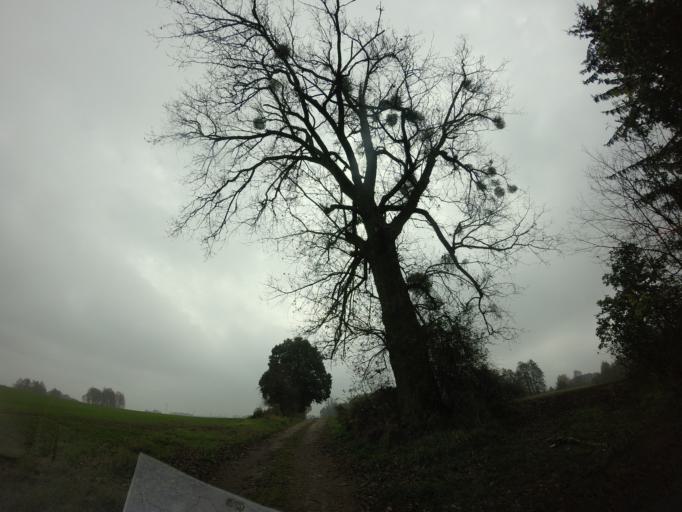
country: PL
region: West Pomeranian Voivodeship
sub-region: Powiat choszczenski
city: Recz
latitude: 53.2358
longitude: 15.5626
